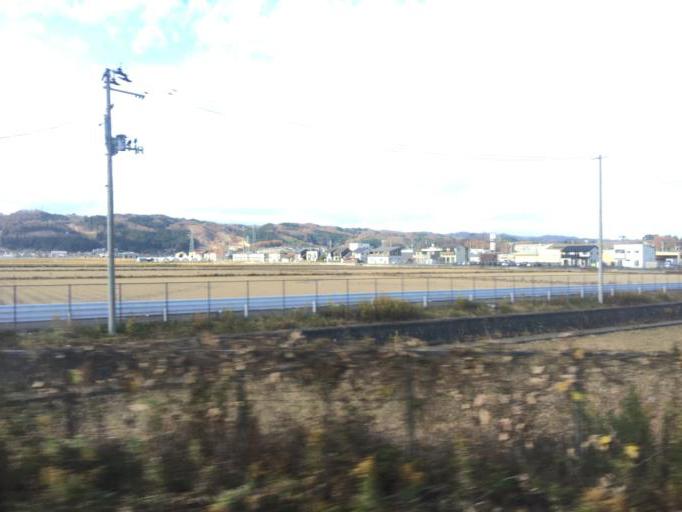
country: JP
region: Miyagi
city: Iwanuma
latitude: 38.1054
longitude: 140.8582
